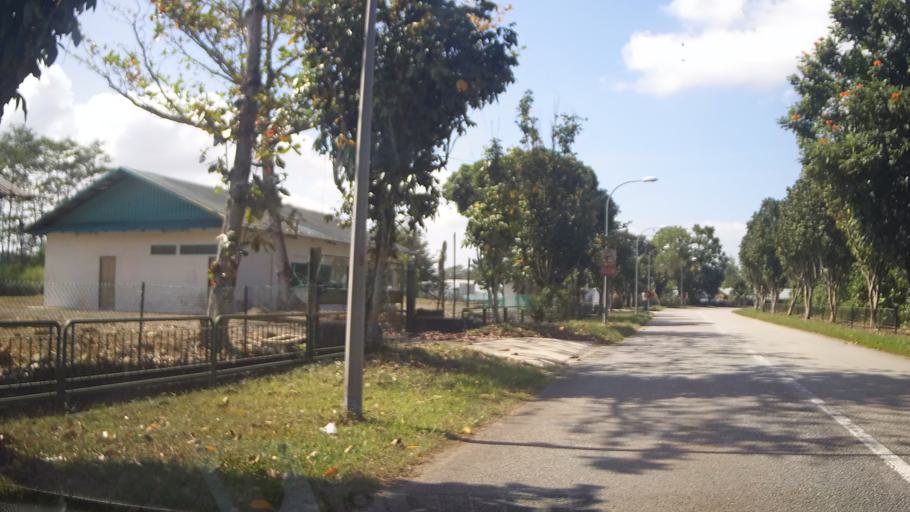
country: MY
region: Johor
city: Johor Bahru
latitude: 1.4338
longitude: 103.7189
